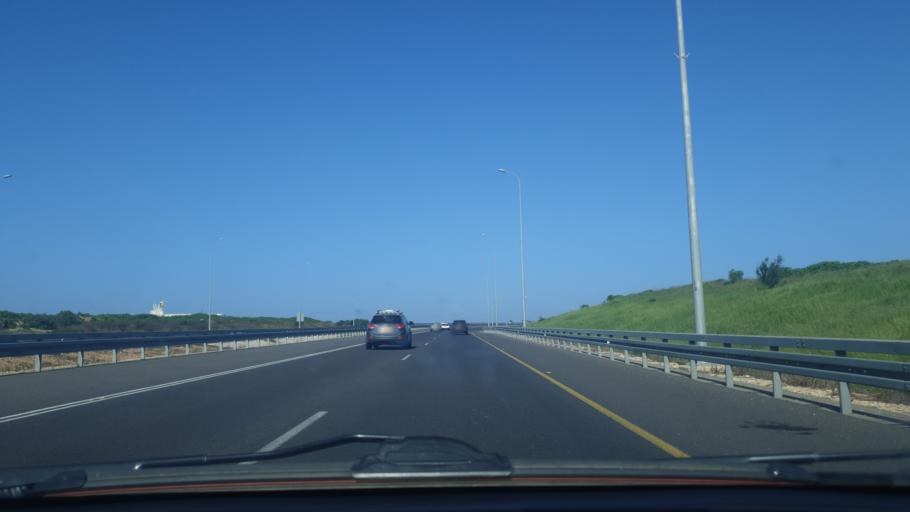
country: IL
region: Tel Aviv
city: Kefar Shemaryahu
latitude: 32.2194
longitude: 34.8349
